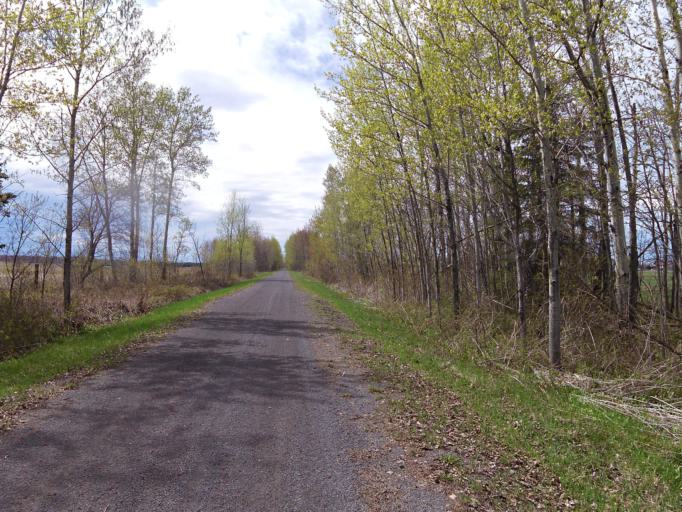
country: CA
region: Ontario
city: Hawkesbury
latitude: 45.5392
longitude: -74.7341
